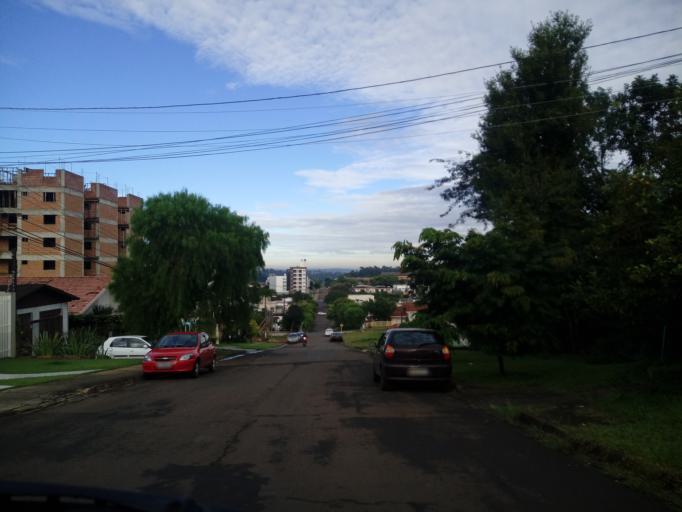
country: BR
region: Santa Catarina
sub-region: Chapeco
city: Chapeco
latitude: -27.1069
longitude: -52.6241
